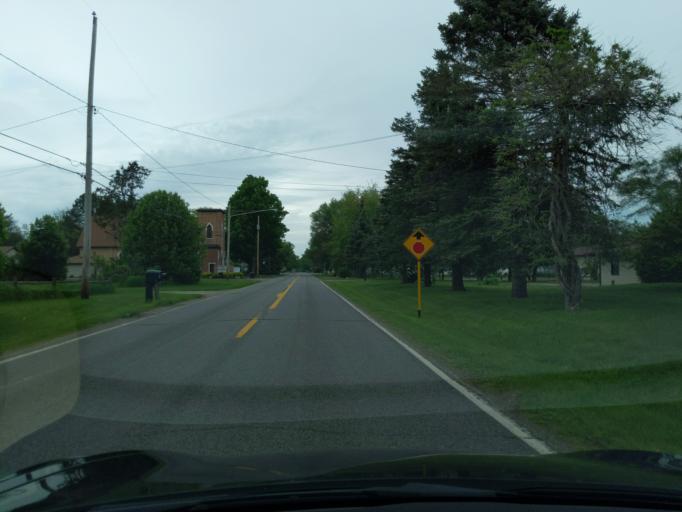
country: US
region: Michigan
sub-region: Ingham County
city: Leslie
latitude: 42.3783
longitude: -84.3492
